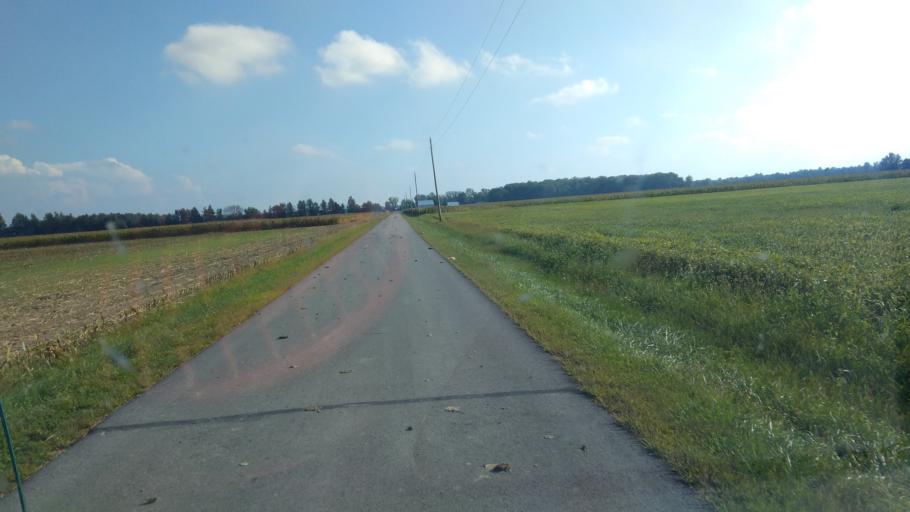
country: US
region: Ohio
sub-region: Hardin County
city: Forest
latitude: 40.7391
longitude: -83.4776
